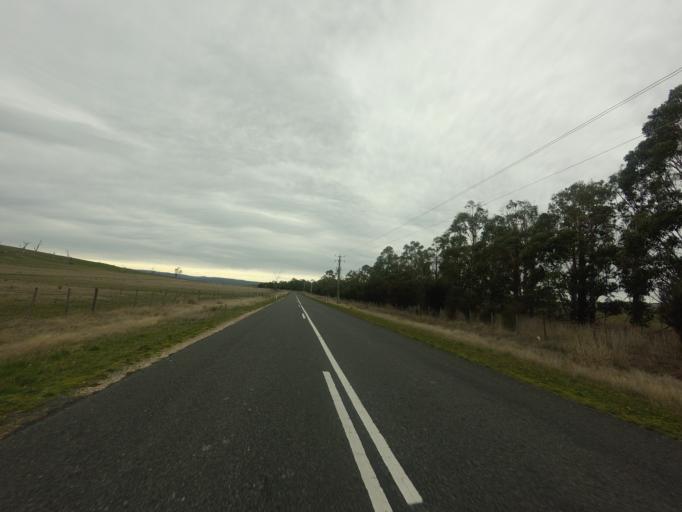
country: AU
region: Tasmania
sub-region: Derwent Valley
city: New Norfolk
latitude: -42.4145
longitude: 147.0059
